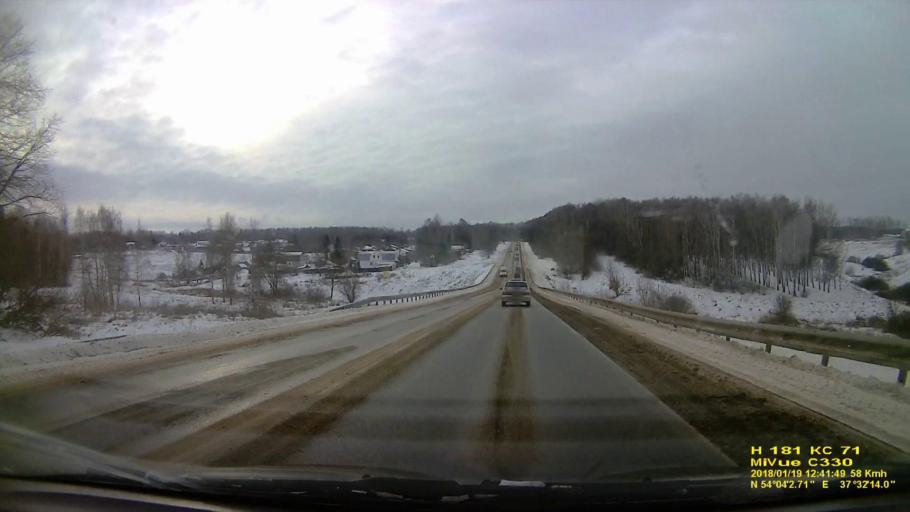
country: RU
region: Tula
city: Pervomayskiy
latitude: 54.0675
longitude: 37.5372
